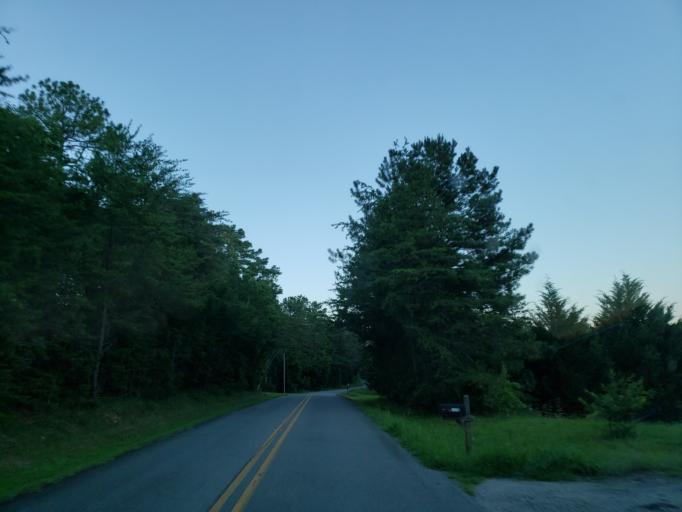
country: US
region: Georgia
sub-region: Bartow County
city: Emerson
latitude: 34.0598
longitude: -84.8328
